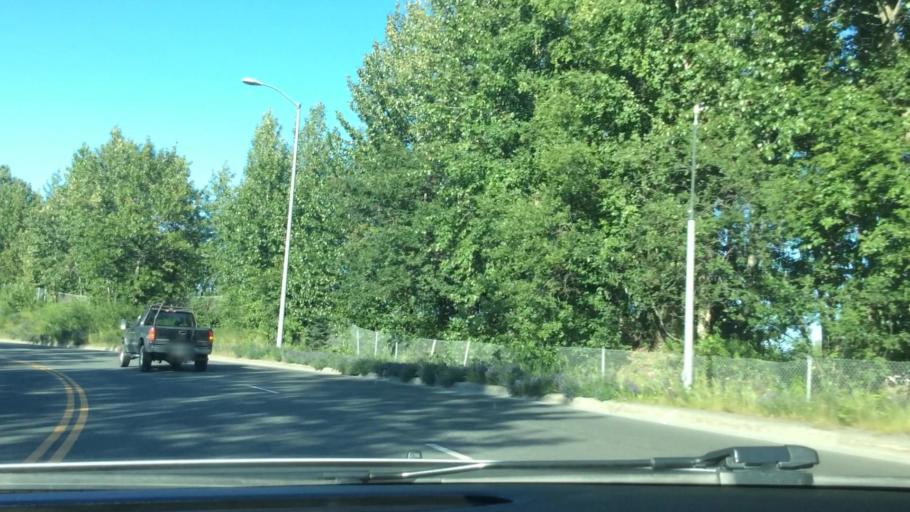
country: US
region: Alaska
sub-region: Anchorage Municipality
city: Anchorage
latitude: 61.2285
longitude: -149.8758
